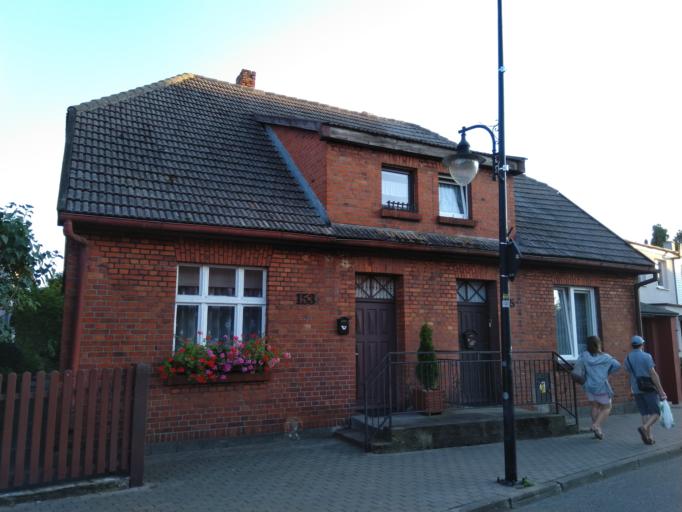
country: PL
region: Pomeranian Voivodeship
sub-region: Powiat pucki
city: Jastarnia
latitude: 54.7023
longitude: 18.6707
